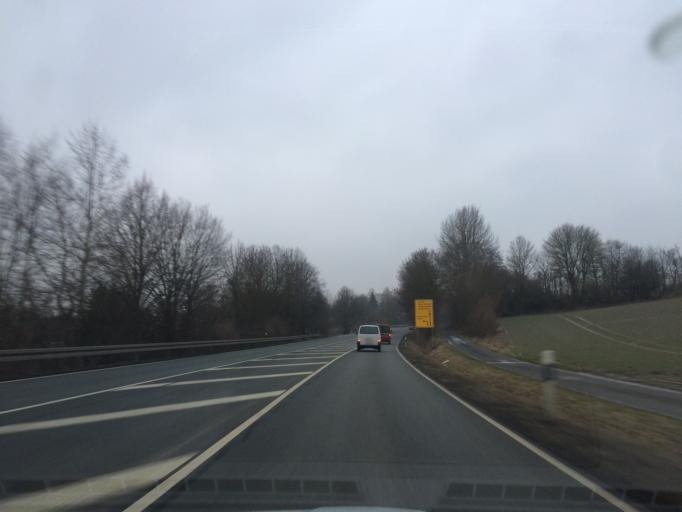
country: DE
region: Hesse
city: Grebenstein
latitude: 51.4557
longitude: 9.4095
